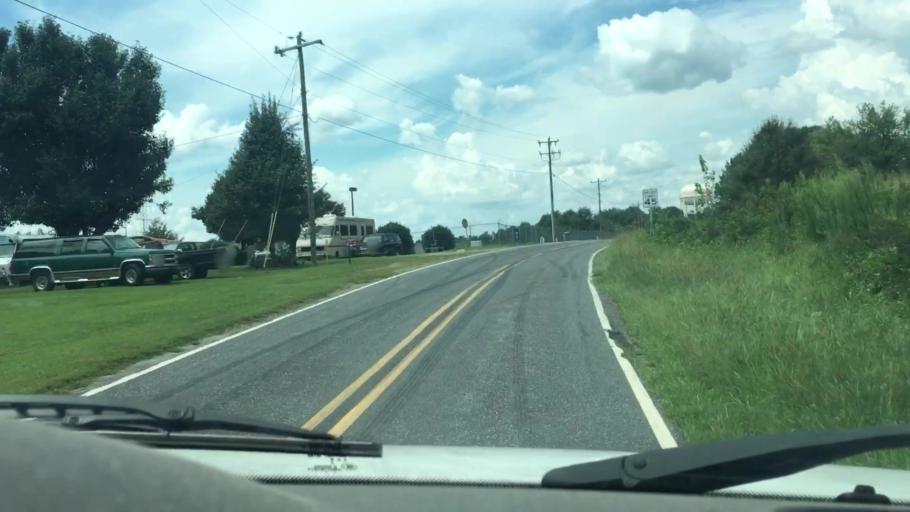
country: US
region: North Carolina
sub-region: Iredell County
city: Troutman
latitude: 35.6769
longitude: -80.8463
